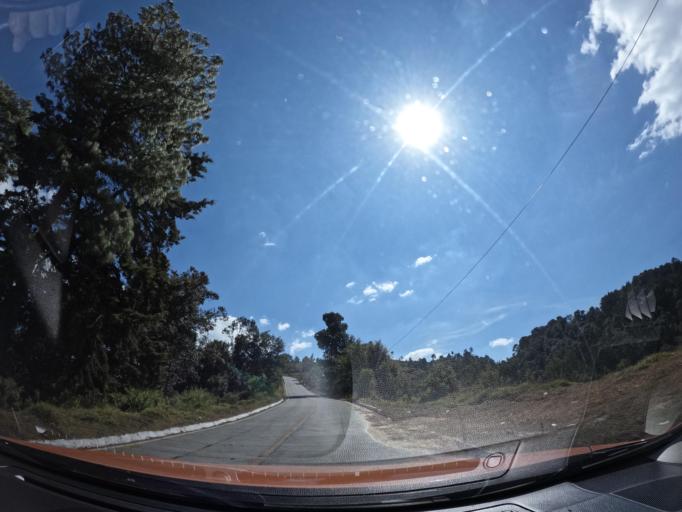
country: GT
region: Chimaltenango
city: Patzun
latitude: 14.6757
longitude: -91.0574
